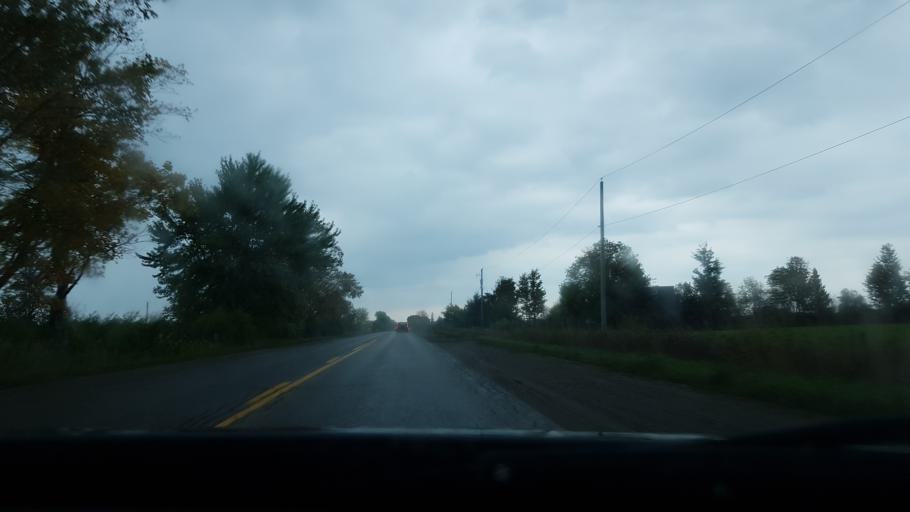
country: CA
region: Ontario
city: Omemee
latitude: 44.3808
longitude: -78.6140
